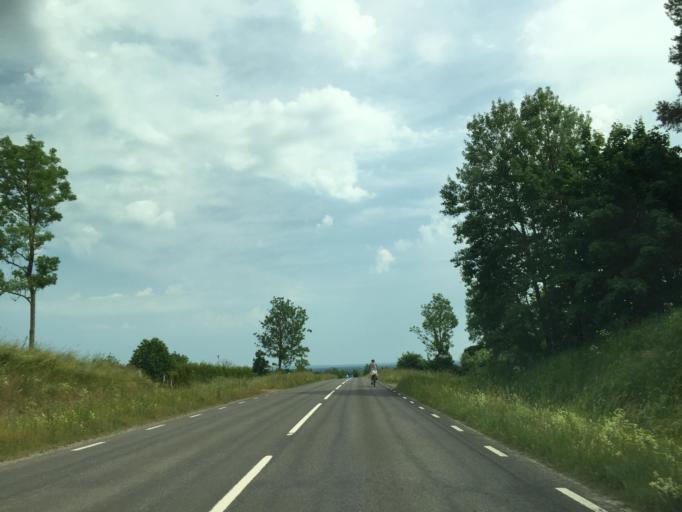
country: SE
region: Vaestra Goetaland
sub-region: Skovde Kommun
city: Skultorp
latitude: 58.3290
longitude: 13.7946
